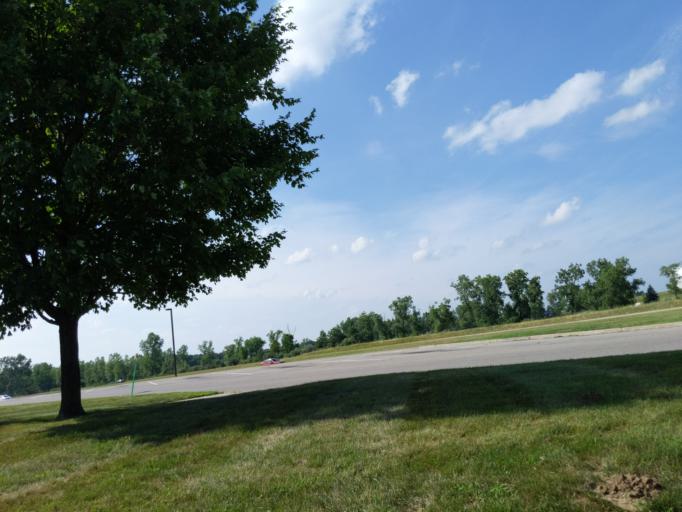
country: US
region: Michigan
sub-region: Livingston County
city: Howell
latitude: 42.6041
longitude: -83.9565
